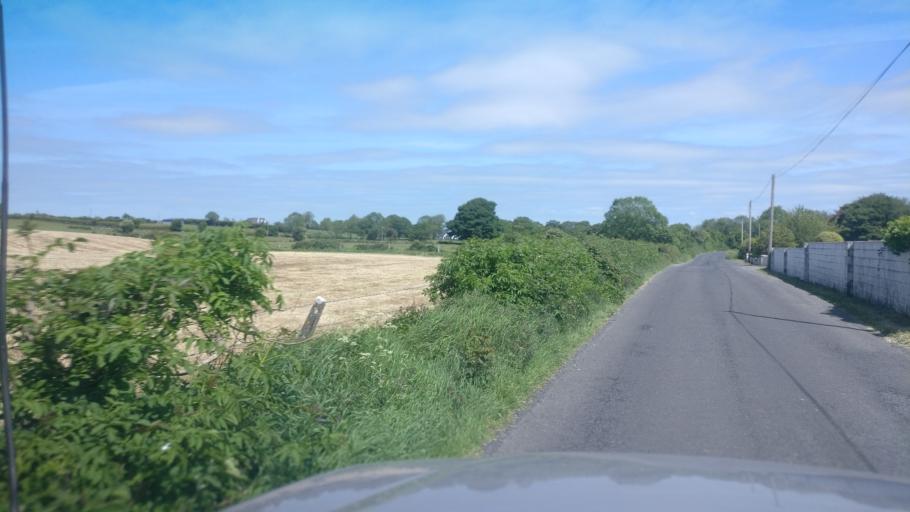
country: IE
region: Connaught
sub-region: County Galway
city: Gort
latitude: 53.1499
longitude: -8.7566
